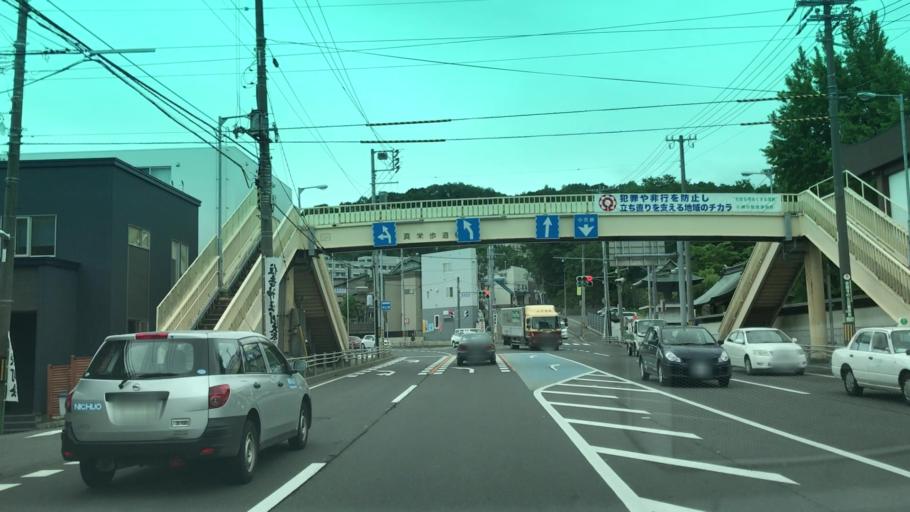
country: JP
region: Hokkaido
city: Otaru
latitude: 43.1811
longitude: 141.0092
